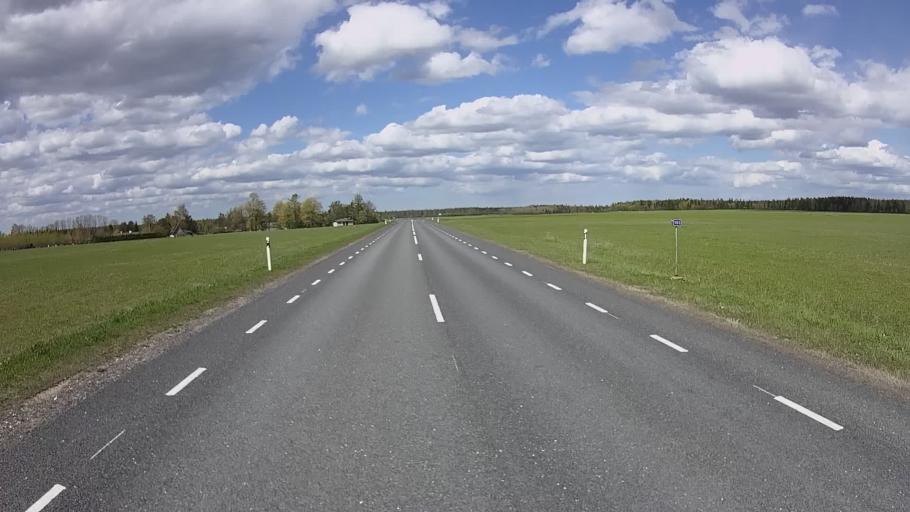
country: EE
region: Jaervamaa
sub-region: Jaerva-Jaani vald
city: Jarva-Jaani
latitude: 59.1131
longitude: 25.7953
